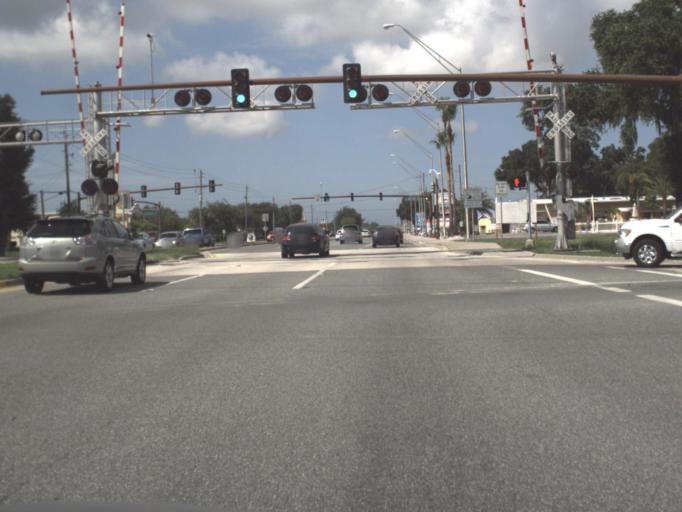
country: US
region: Florida
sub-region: Sarasota County
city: Bee Ridge
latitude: 27.2693
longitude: -82.4799
